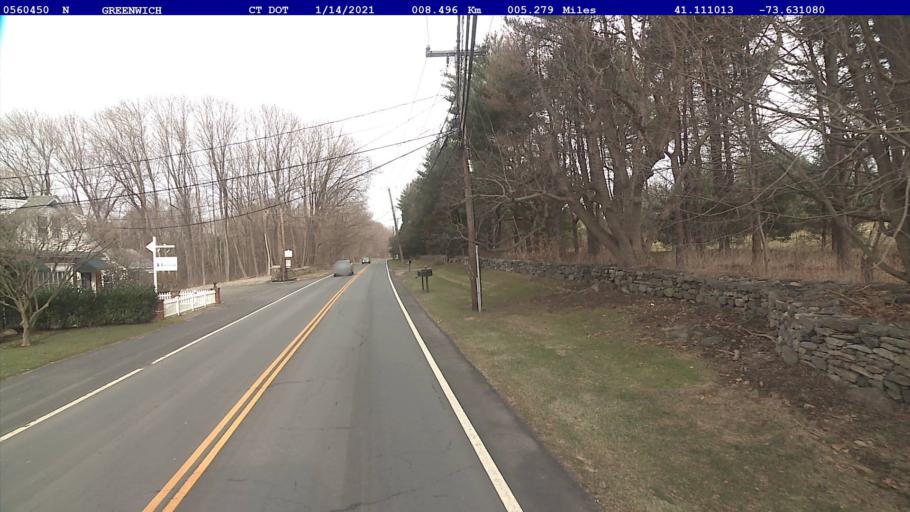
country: US
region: Connecticut
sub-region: Fairfield County
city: Glenville
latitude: 41.1110
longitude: -73.6311
